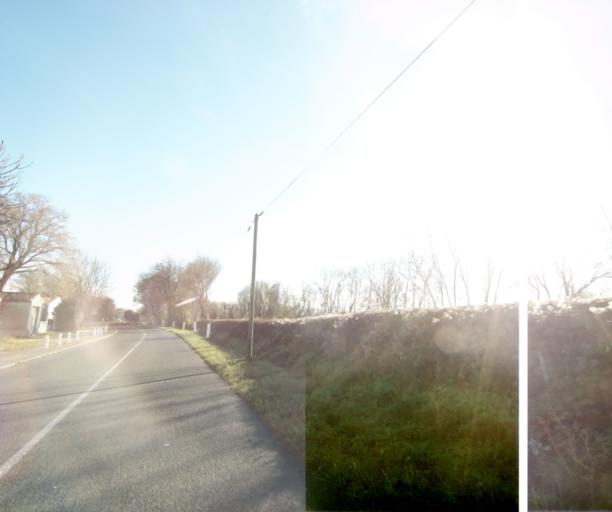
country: FR
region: Poitou-Charentes
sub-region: Departement de la Charente-Maritime
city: Chaniers
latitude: 45.7277
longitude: -0.5849
